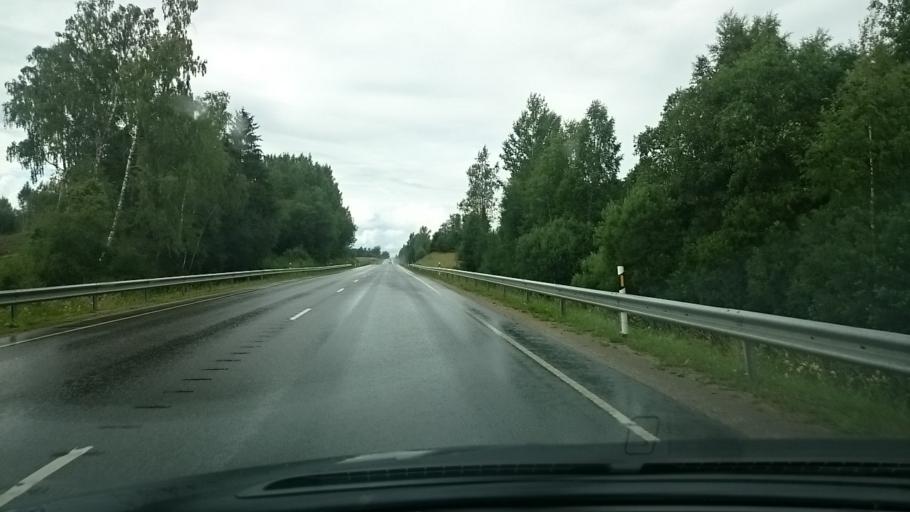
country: EE
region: Tartu
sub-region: UElenurme vald
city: Ulenurme
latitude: 58.1336
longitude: 26.7197
